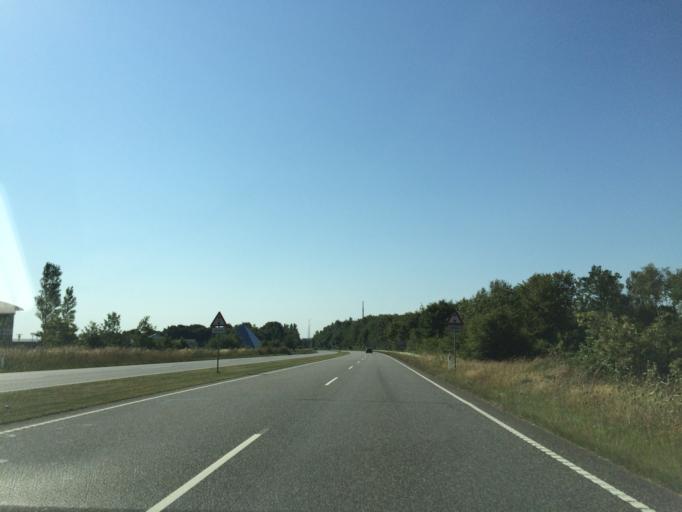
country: DK
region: South Denmark
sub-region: Kolding Kommune
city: Kolding
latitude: 55.5140
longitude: 9.5021
